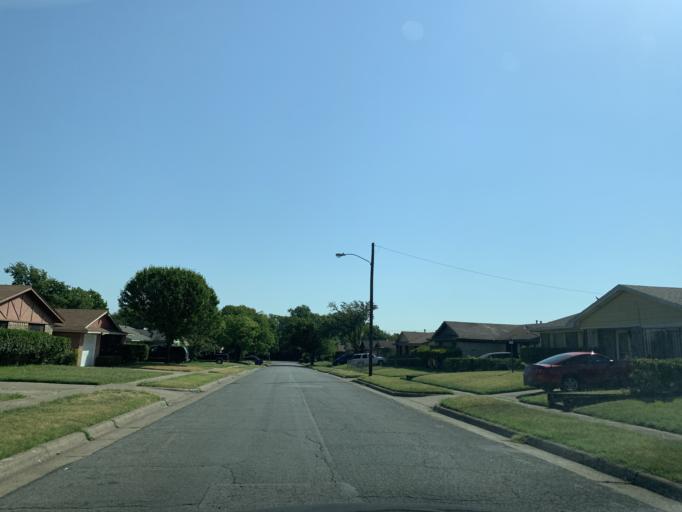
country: US
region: Texas
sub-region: Dallas County
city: Hutchins
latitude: 32.6677
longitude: -96.7619
